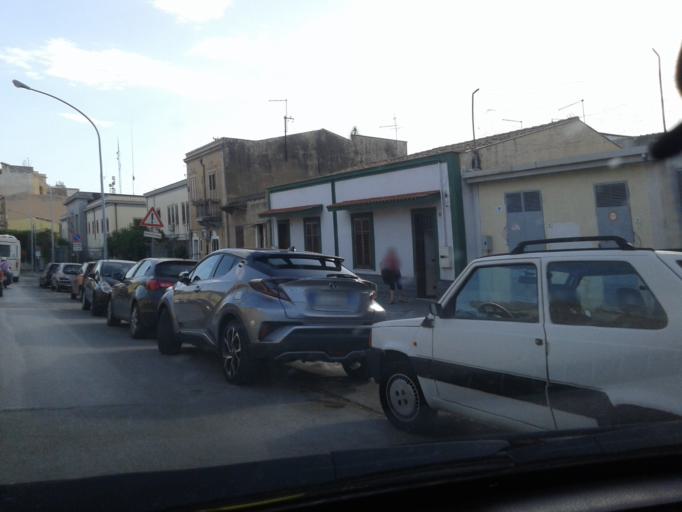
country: IT
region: Sicily
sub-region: Palermo
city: Palermo
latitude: 38.1025
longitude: 13.3399
